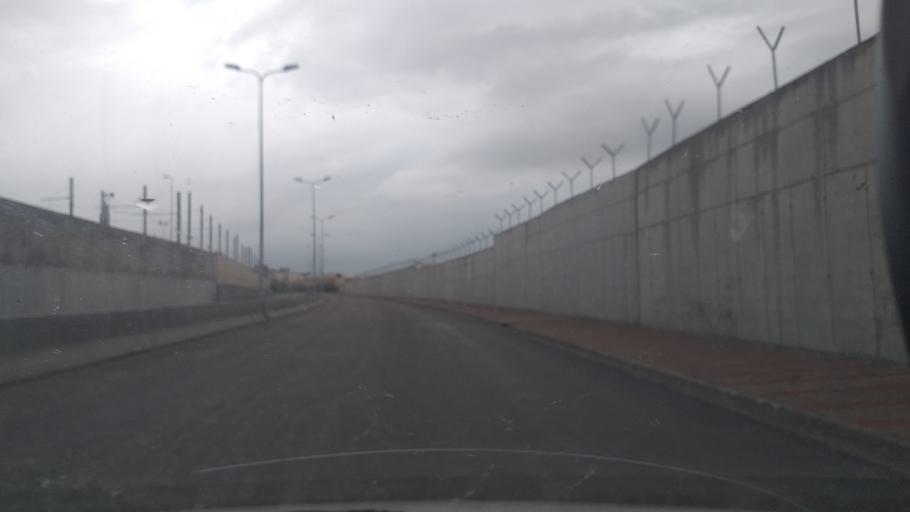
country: TN
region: Ariana
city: Ariana
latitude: 36.8573
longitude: 10.2137
